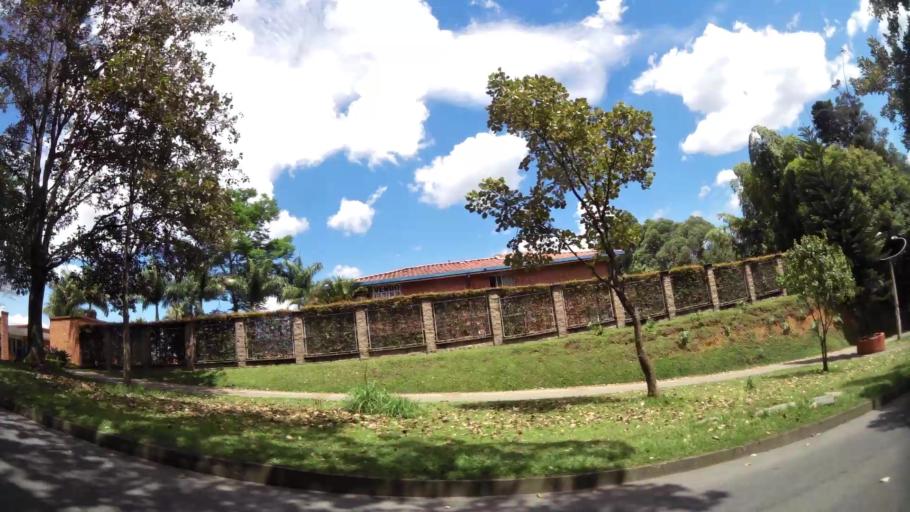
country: CO
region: Antioquia
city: Sabaneta
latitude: 6.1593
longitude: -75.6284
